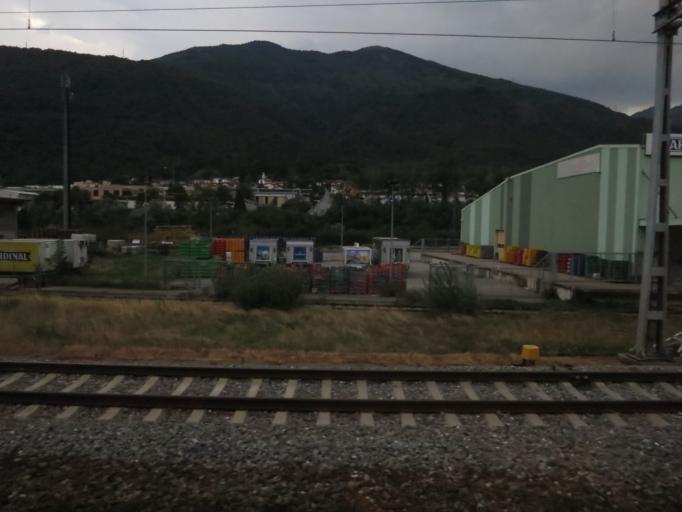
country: CH
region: Ticino
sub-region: Lugano District
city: Gravesano
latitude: 46.0529
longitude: 8.9287
